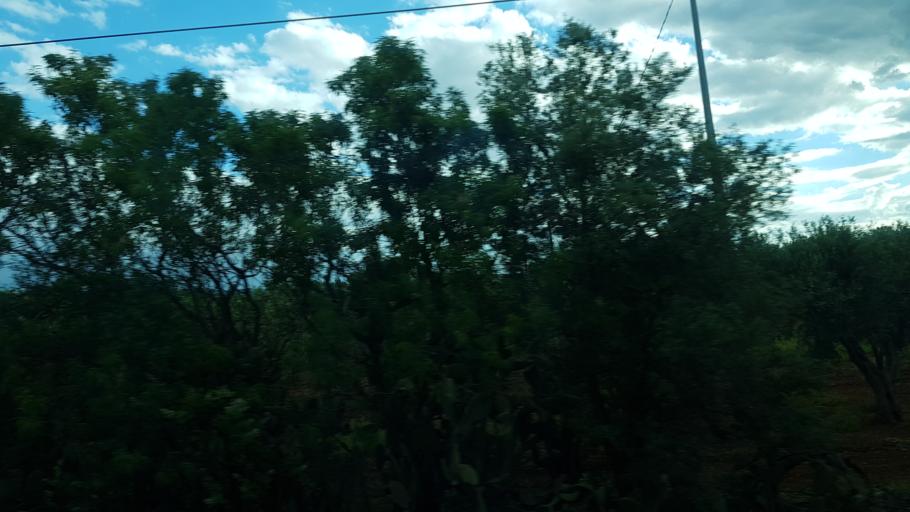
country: IT
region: Apulia
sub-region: Provincia di Brindisi
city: Pezze di Greco
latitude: 40.8419
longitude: 17.4021
